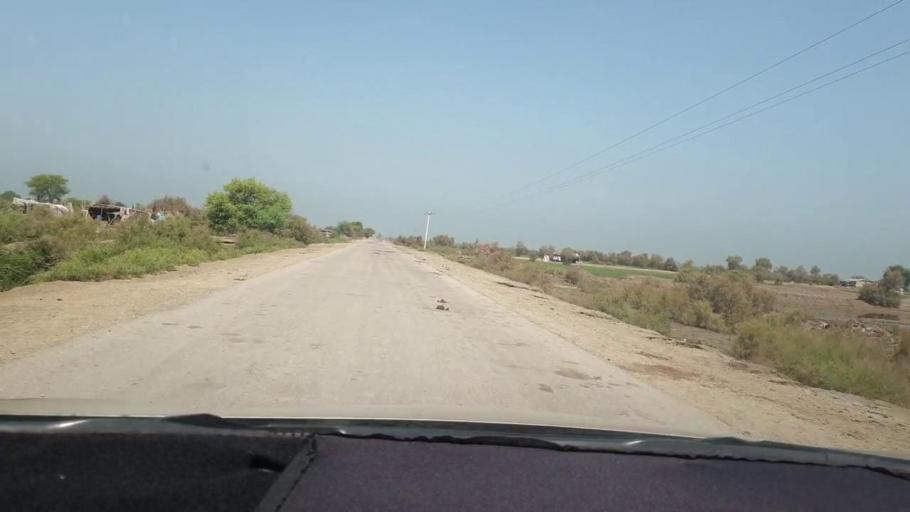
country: PK
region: Sindh
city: Miro Khan
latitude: 27.8255
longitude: 68.0194
